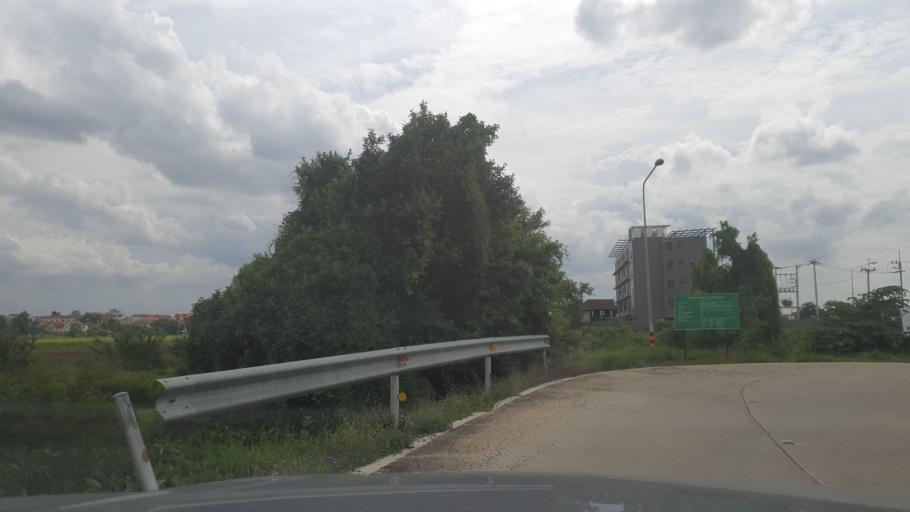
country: TH
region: Pathum Thani
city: Lam Luk Ka
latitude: 13.9391
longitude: 100.7242
